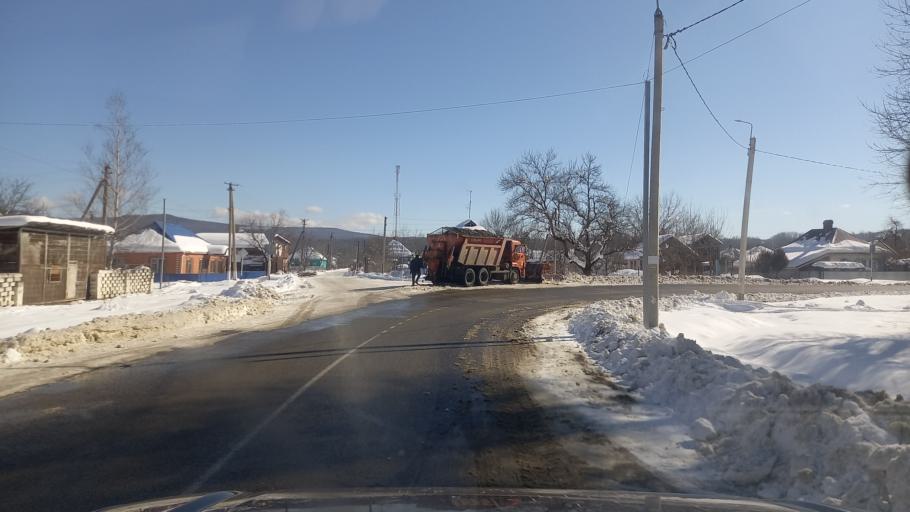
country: RU
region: Adygeya
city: Abadzekhskaya
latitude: 44.3915
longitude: 40.2207
